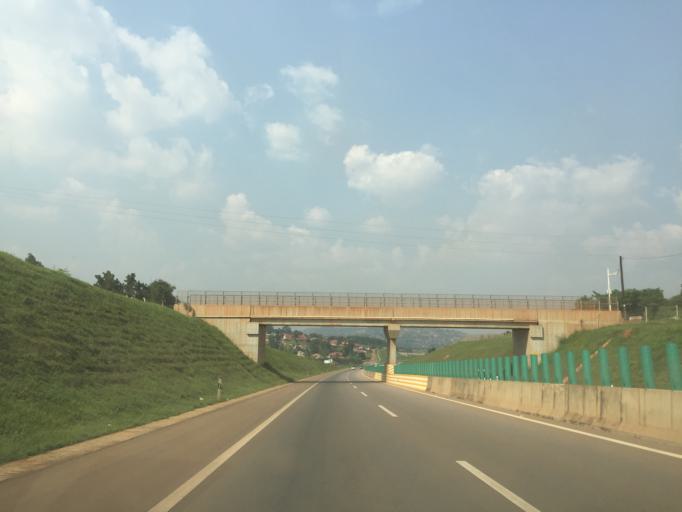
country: UG
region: Central Region
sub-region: Wakiso District
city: Kajansi
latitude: 0.1970
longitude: 32.5260
